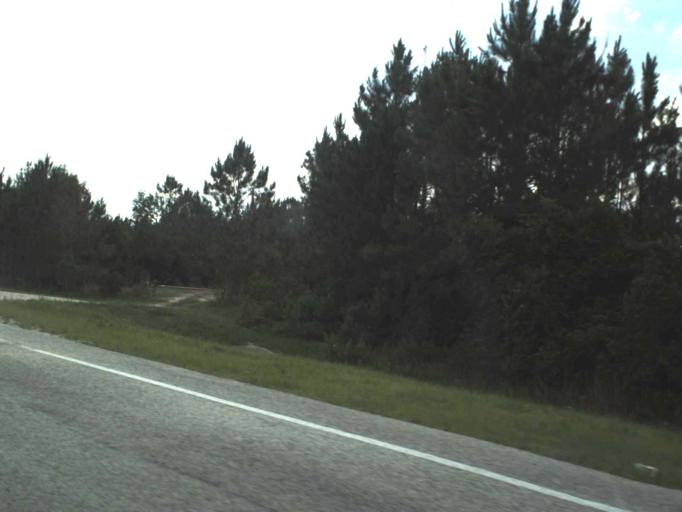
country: US
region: Florida
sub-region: Volusia County
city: Samsula-Spruce Creek
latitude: 29.0251
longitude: -81.1279
